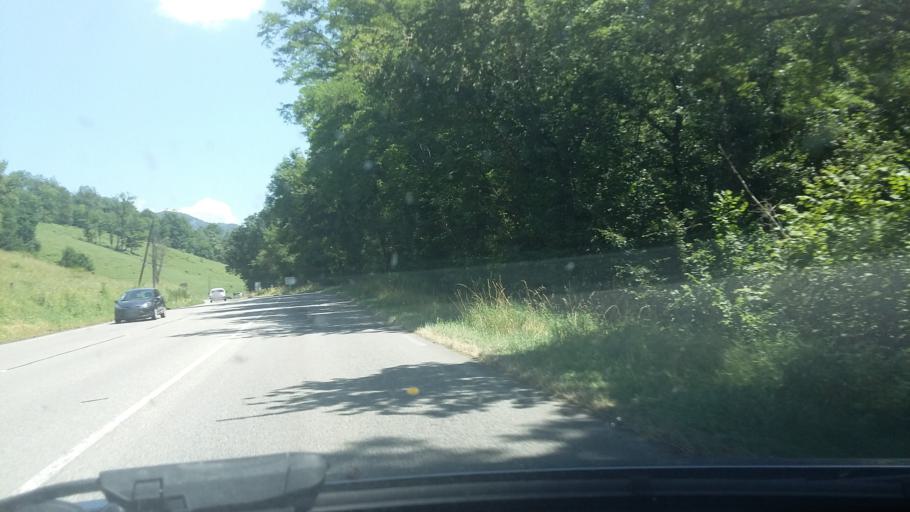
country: FR
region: Rhone-Alpes
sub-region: Departement de la Savoie
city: Yenne
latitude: 45.7036
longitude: 5.7843
